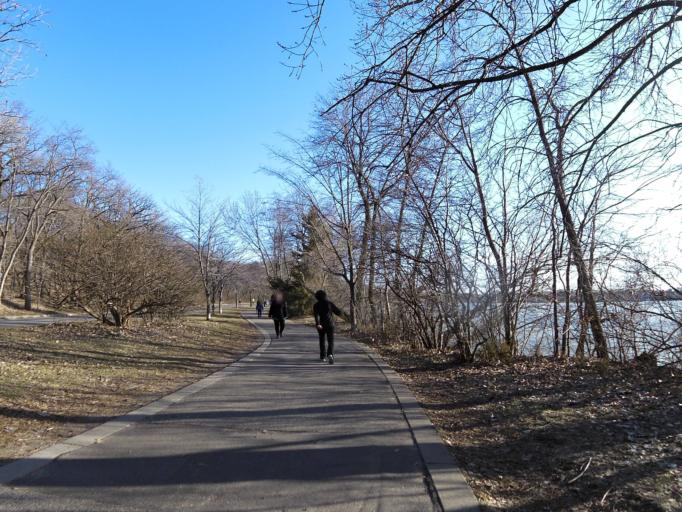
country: US
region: Minnesota
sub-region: Hennepin County
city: Richfield
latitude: 44.9248
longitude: -93.2968
